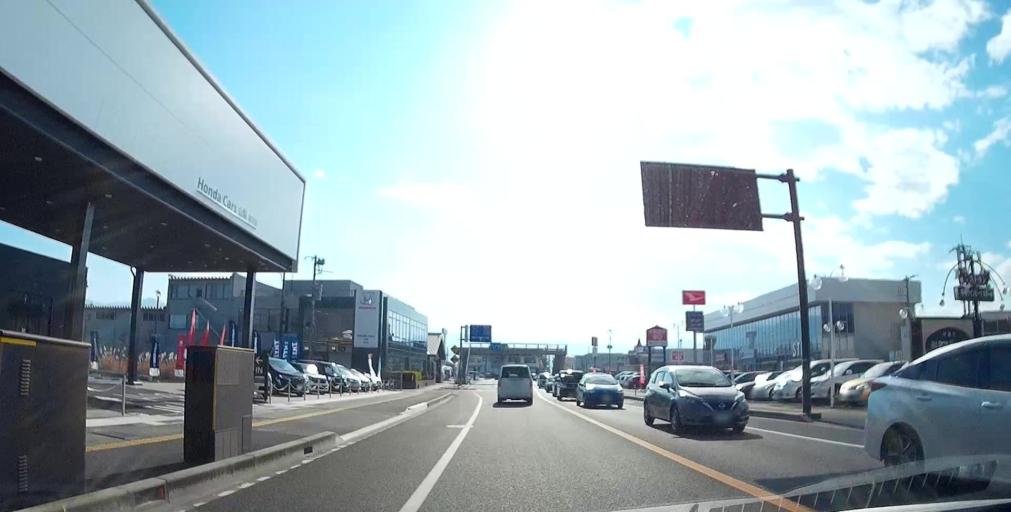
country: JP
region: Yamanashi
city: Isawa
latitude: 35.6476
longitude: 138.6126
